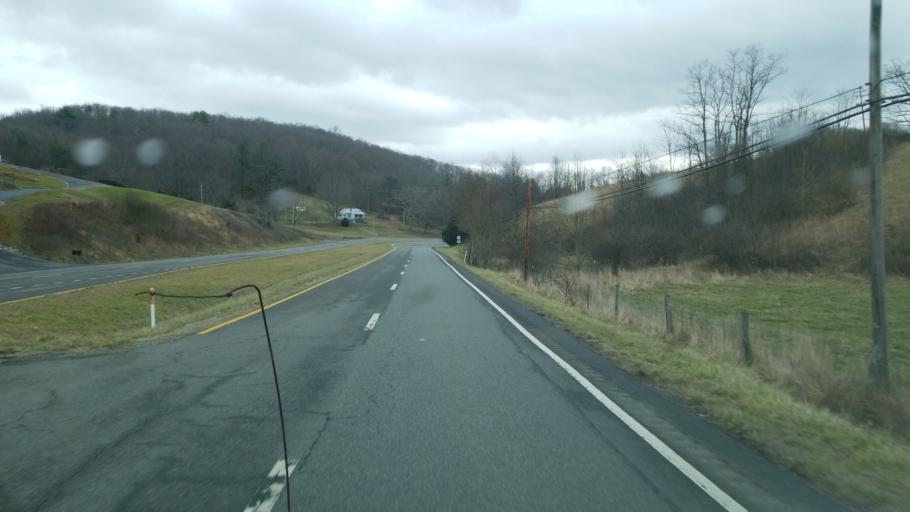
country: US
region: Virginia
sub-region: Giles County
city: Pearisburg
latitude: 37.2828
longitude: -80.7436
